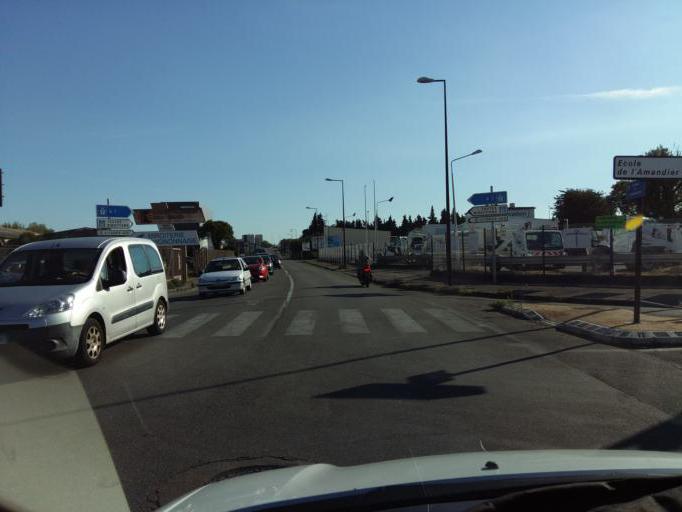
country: FR
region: Provence-Alpes-Cote d'Azur
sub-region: Departement du Vaucluse
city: Montfavet
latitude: 43.9379
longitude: 4.8495
